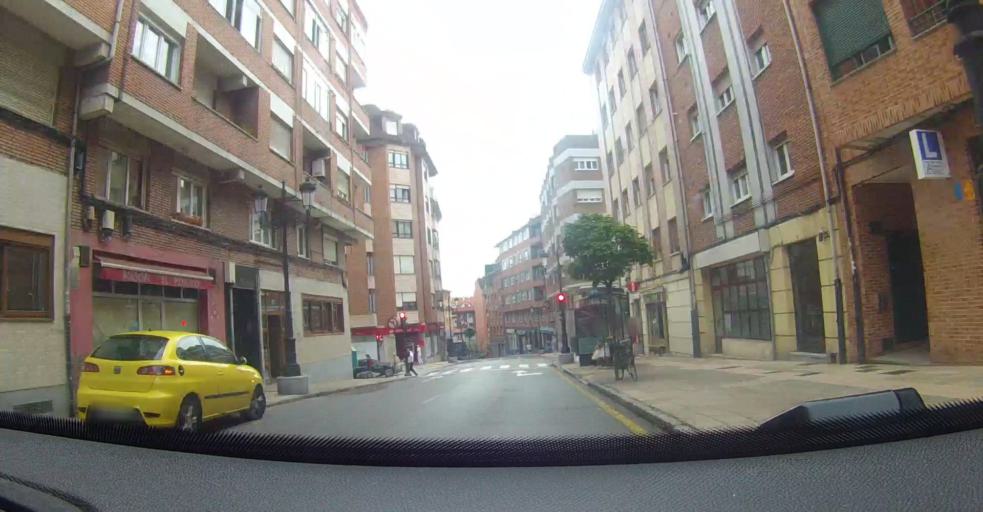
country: ES
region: Asturias
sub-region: Province of Asturias
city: Oviedo
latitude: 43.3698
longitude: -5.8555
